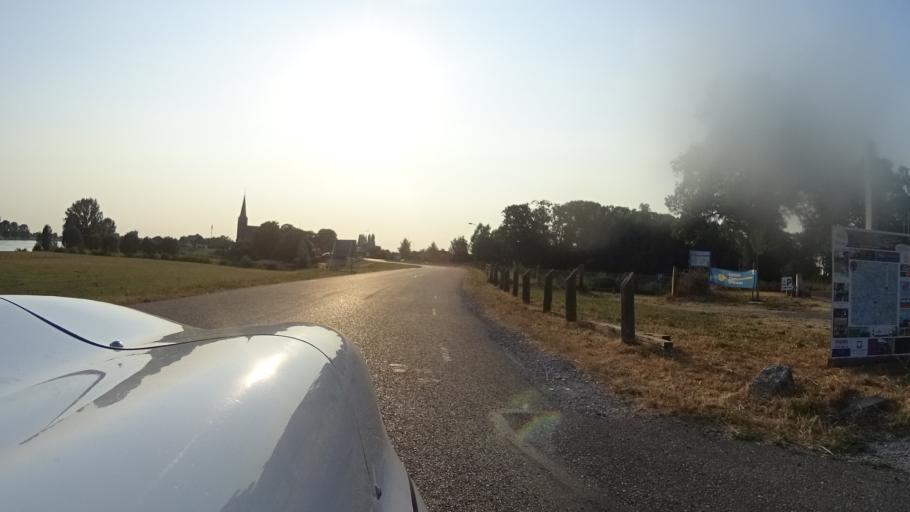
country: NL
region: Gelderland
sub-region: Gemeente Druten
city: Druten
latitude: 51.8311
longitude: 5.5912
